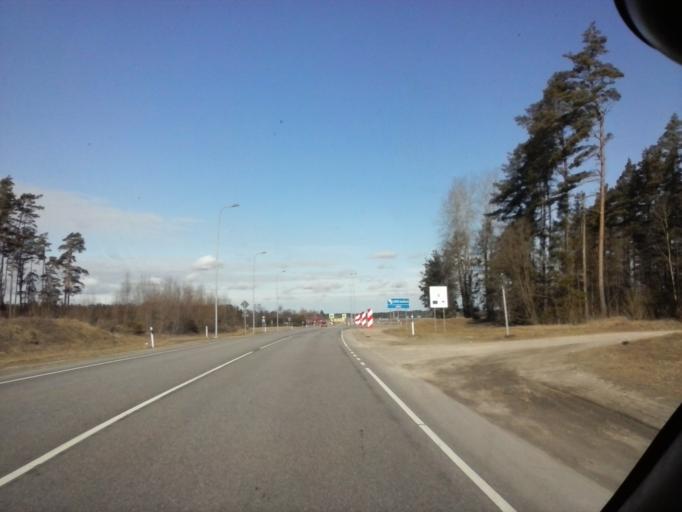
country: EE
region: Harju
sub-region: Raasiku vald
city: Raasiku
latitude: 59.1702
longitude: 25.1584
